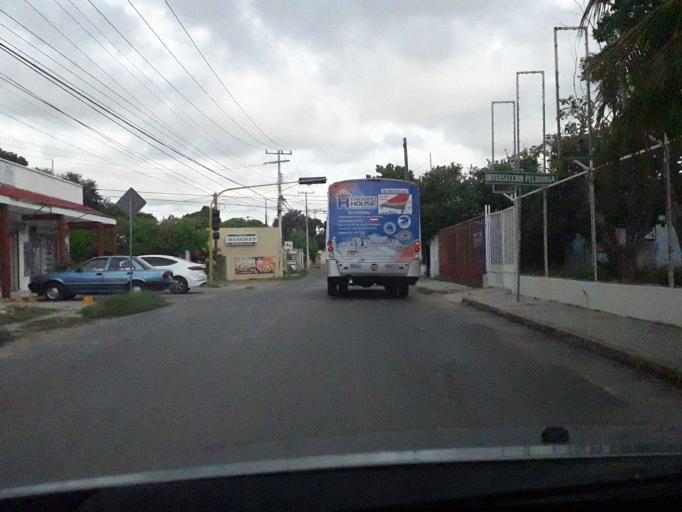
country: MX
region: Yucatan
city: Merida
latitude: 21.0206
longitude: -89.6381
